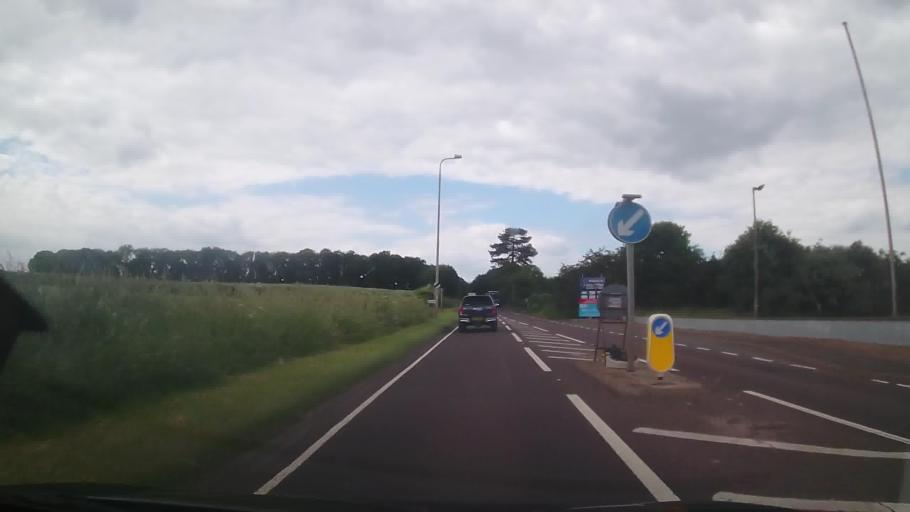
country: GB
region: England
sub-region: Herefordshire
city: Wellington
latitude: 52.1143
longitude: -2.7317
